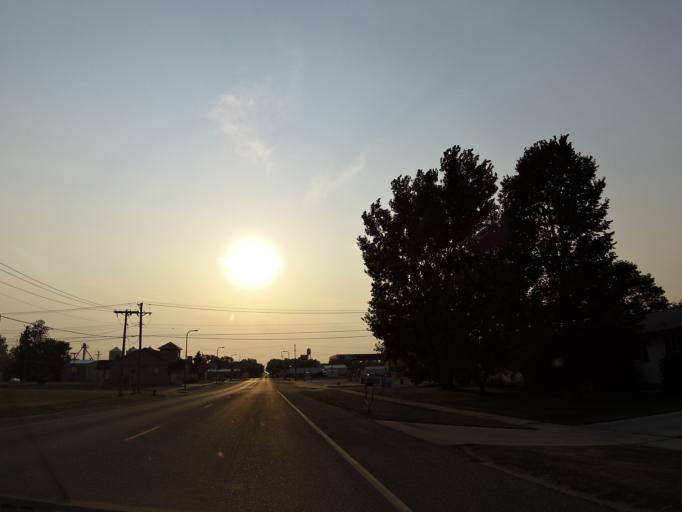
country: US
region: North Dakota
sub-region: Traill County
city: Mayville
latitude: 47.4985
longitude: -97.3670
